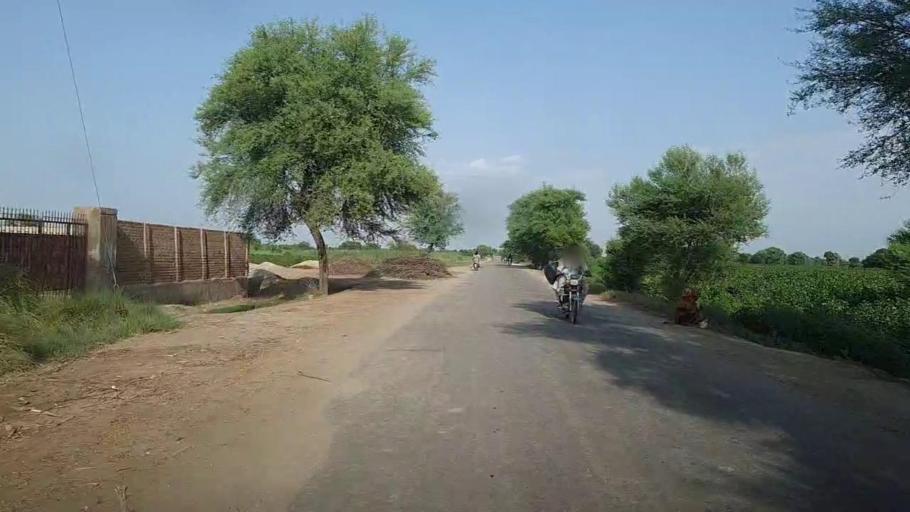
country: PK
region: Sindh
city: Khairpur
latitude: 28.0766
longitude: 69.7987
